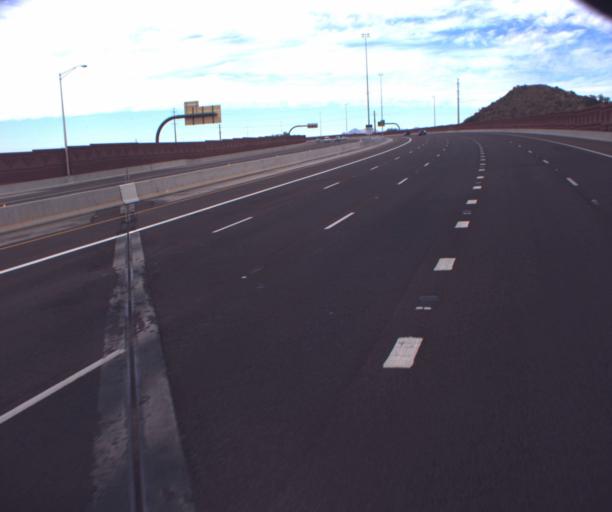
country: US
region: Arizona
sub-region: Pinal County
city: Apache Junction
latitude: 33.4282
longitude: -111.6362
